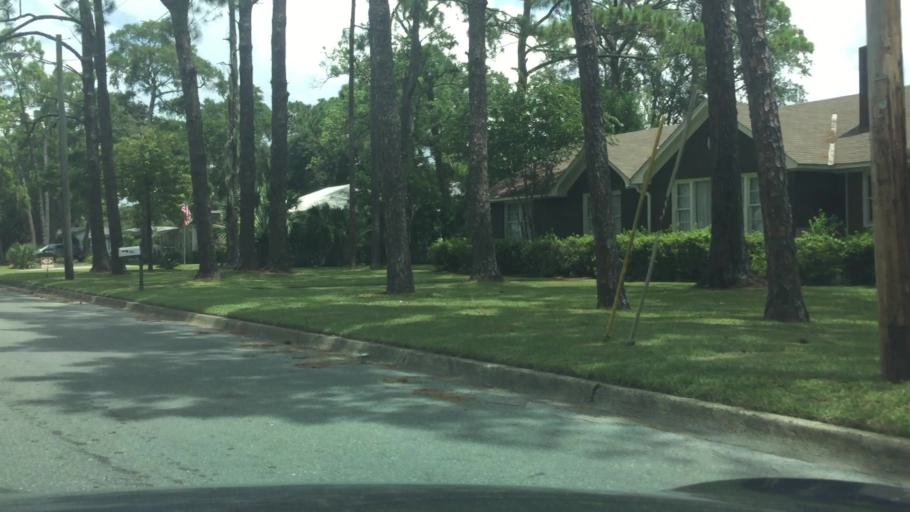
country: US
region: Florida
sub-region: Bay County
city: Panama City
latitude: 30.1460
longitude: -85.6503
